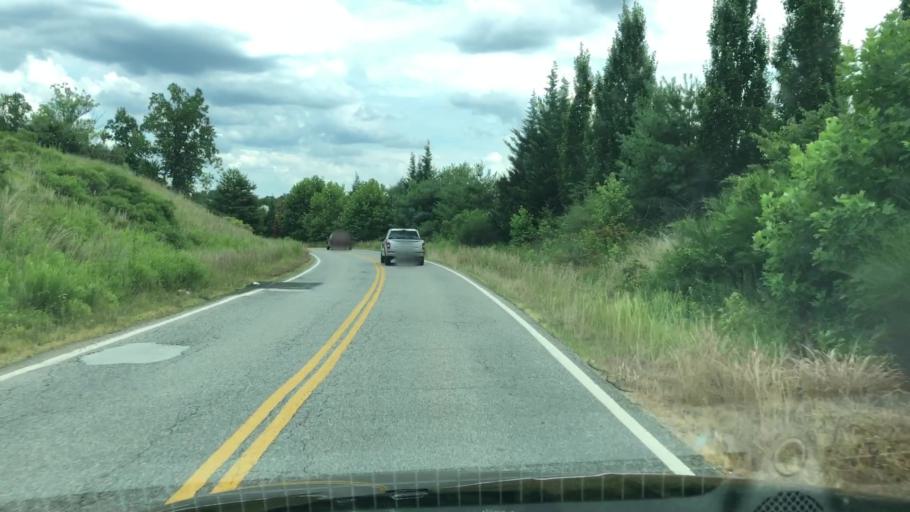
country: US
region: Virginia
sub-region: Stafford County
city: Falmouth
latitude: 38.3374
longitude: -77.5168
